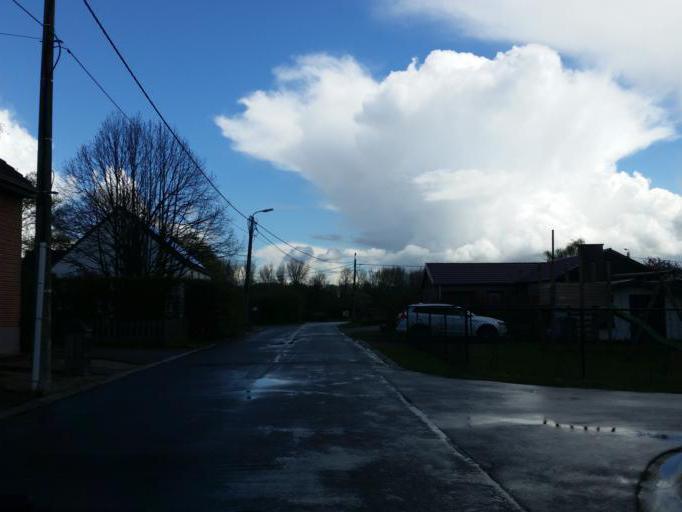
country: BE
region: Flanders
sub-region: Provincie Vlaams-Brabant
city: Boortmeerbeek
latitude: 50.9836
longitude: 4.5341
